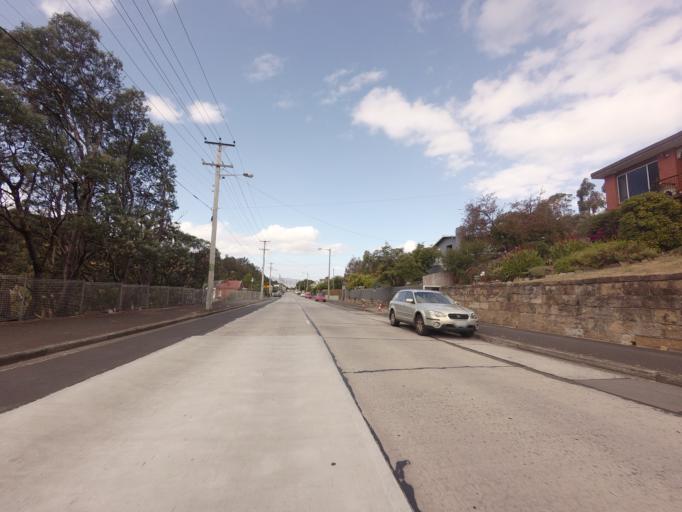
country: AU
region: Tasmania
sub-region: Hobart
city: Dynnyrne
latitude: -42.8956
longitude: 147.2972
